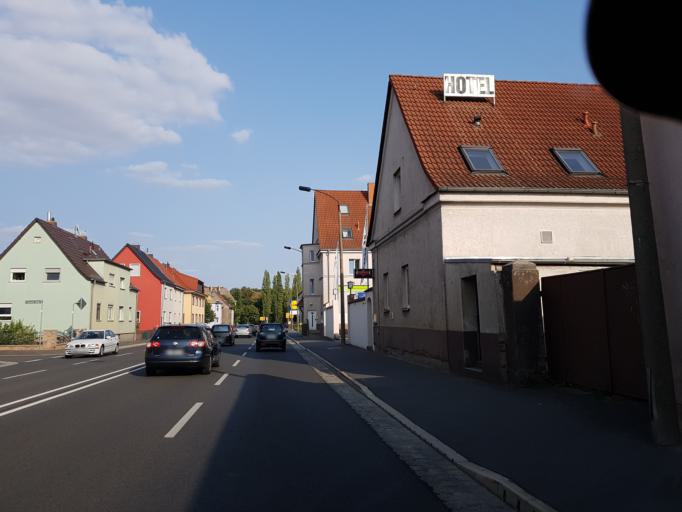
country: DE
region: Saxony
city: Torgau
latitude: 51.5592
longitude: 12.9891
